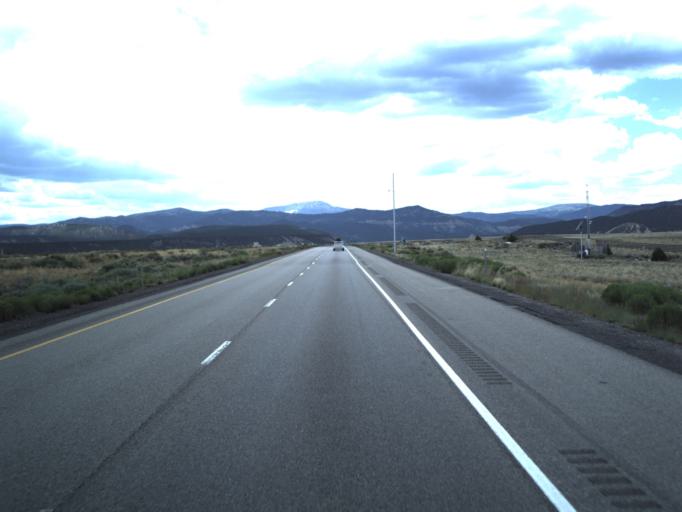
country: US
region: Utah
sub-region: Emery County
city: Ferron
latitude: 38.7790
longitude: -111.3152
